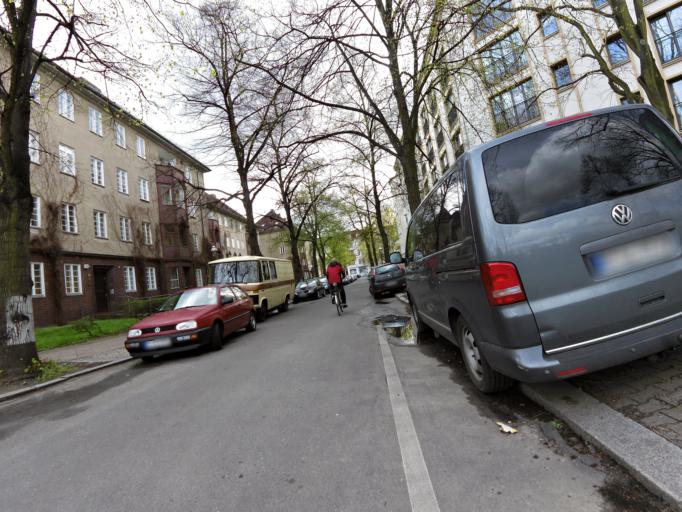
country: DE
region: Berlin
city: Schmargendorf
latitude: 52.4745
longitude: 13.2986
